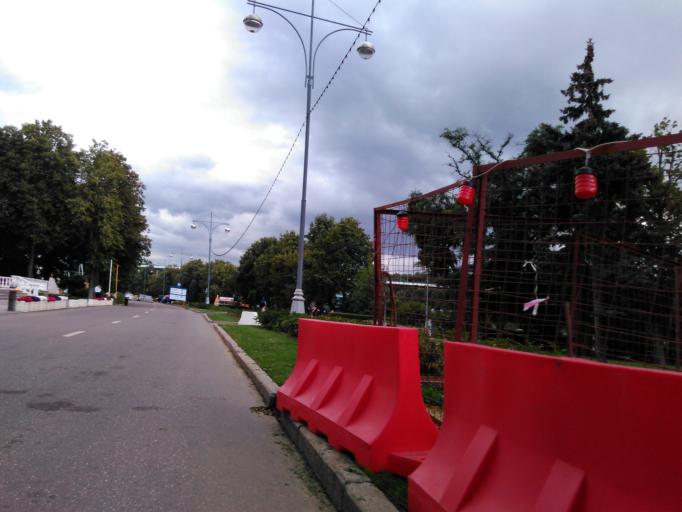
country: RU
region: Moscow
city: Luzhniki
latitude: 55.7124
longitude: 37.5523
